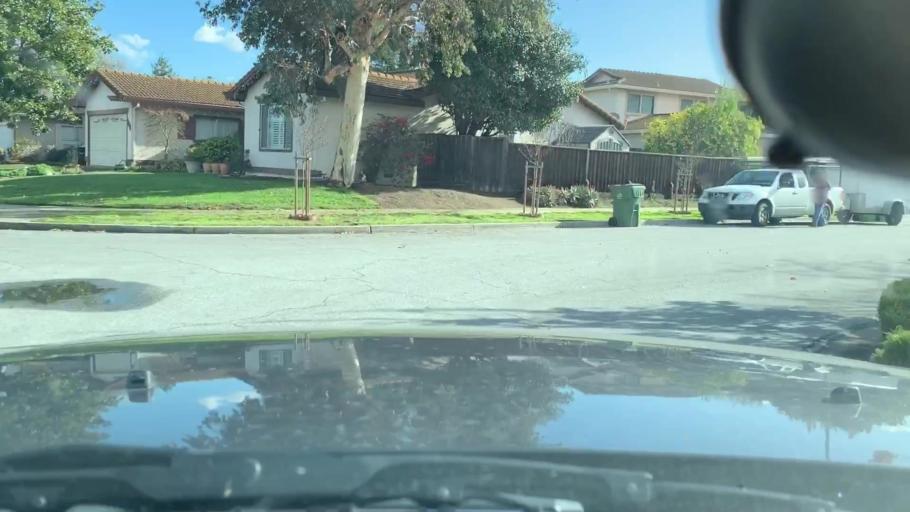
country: US
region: California
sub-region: Santa Clara County
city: Cupertino
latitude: 37.3115
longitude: -121.9931
